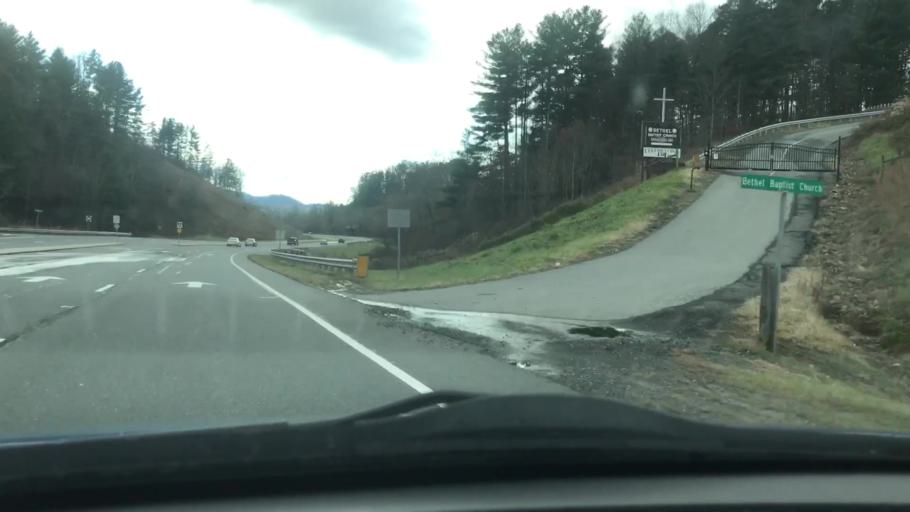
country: US
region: North Carolina
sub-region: Madison County
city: Mars Hill
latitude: 35.8830
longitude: -82.4783
